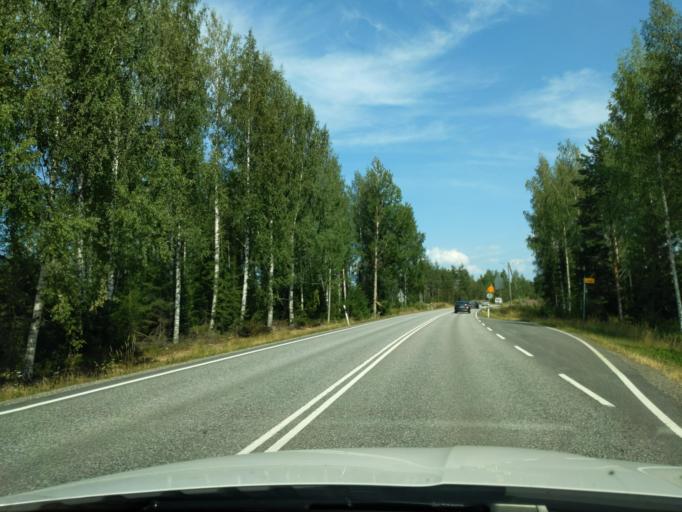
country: FI
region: Paijanne Tavastia
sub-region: Lahti
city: Padasjoki
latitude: 61.3352
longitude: 25.2211
